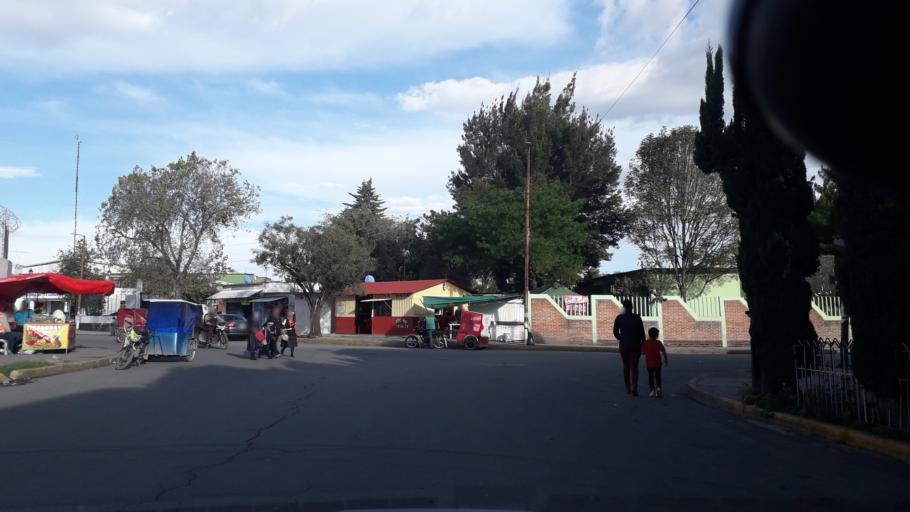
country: MX
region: Mexico
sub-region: Jaltenco
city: Alborada Jaltenco
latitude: 19.6613
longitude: -99.0685
